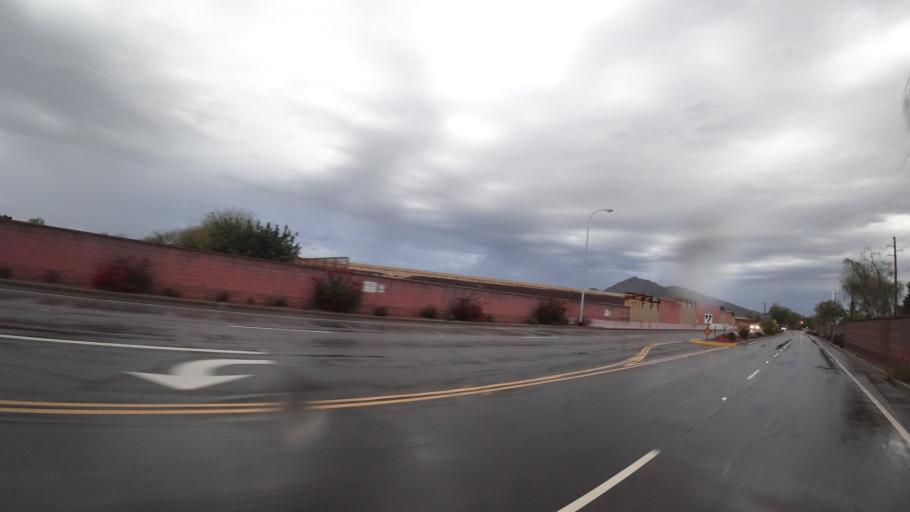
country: US
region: Arizona
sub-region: Maricopa County
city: Paradise Valley
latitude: 33.4769
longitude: -111.9434
